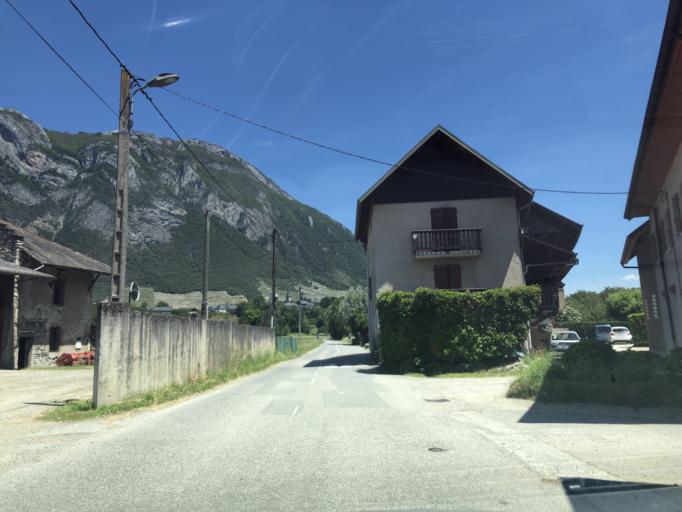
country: FR
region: Rhone-Alpes
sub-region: Departement de la Savoie
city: Montmelian
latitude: 45.4941
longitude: 6.0289
